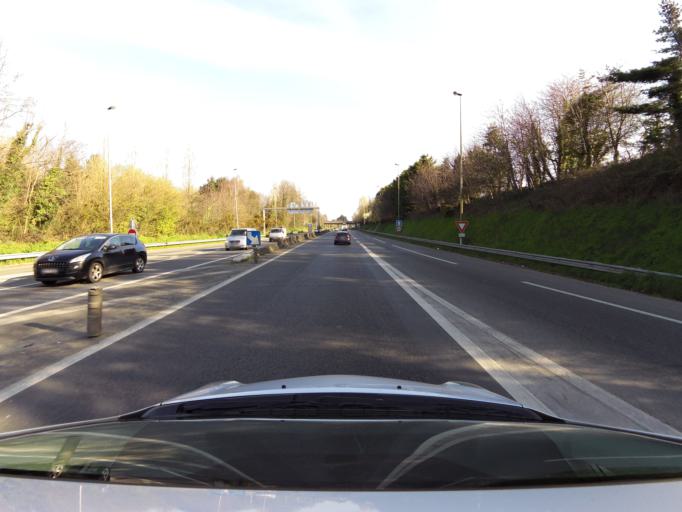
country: FR
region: Brittany
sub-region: Departement du Morbihan
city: Lorient
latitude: 47.7493
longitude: -3.3870
